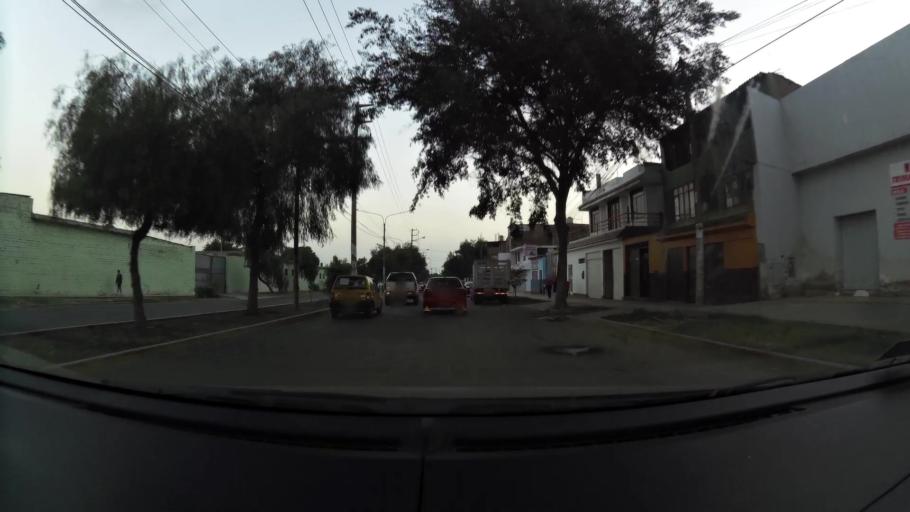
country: PE
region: La Libertad
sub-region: Provincia de Trujillo
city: El Porvenir
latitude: -8.0940
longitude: -79.0187
